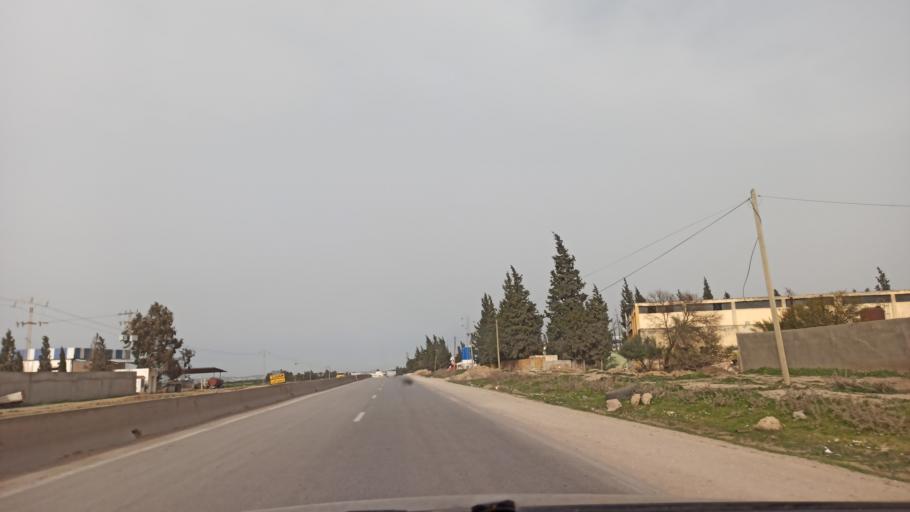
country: TN
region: Tunis
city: La Mohammedia
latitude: 36.5733
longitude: 10.0887
